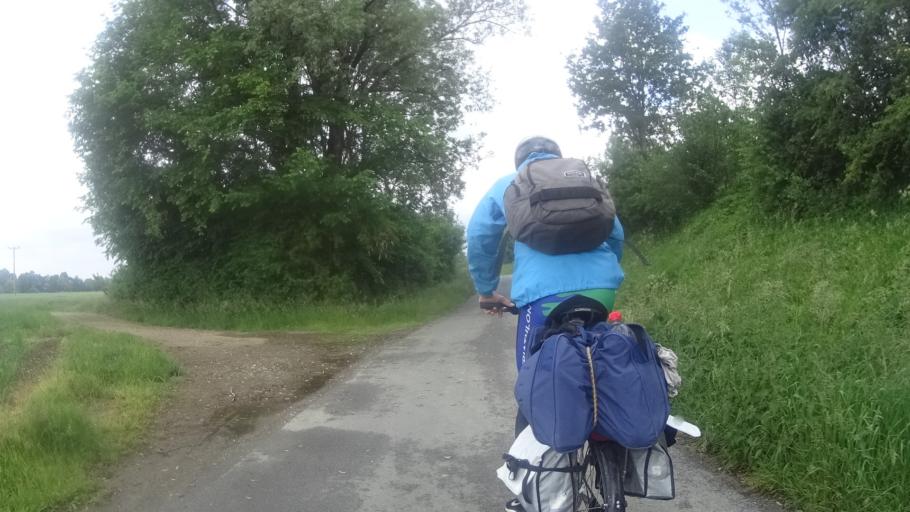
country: DE
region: Bavaria
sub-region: Lower Bavaria
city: Bad Birnbach
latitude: 48.4439
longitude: 13.0616
